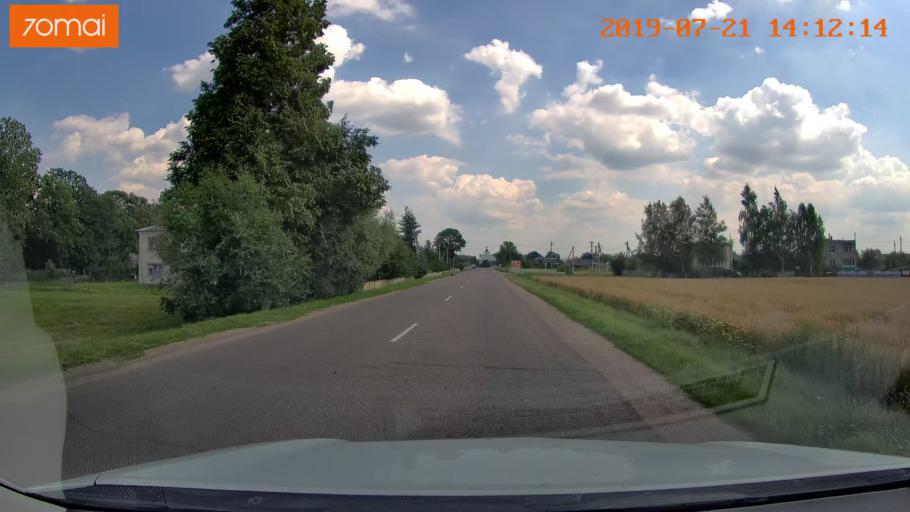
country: BY
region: Grodnenskaya
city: Karelichy
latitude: 53.6533
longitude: 26.1655
